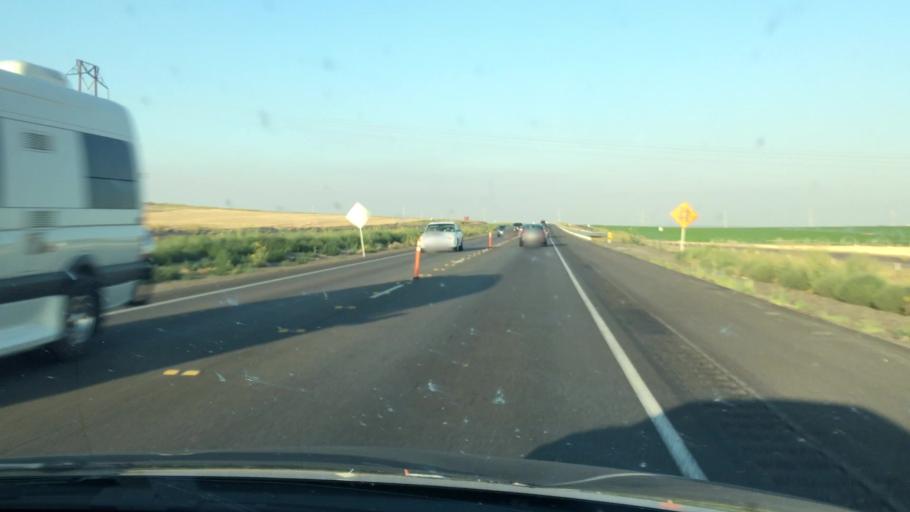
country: US
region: Idaho
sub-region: Twin Falls County
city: Hansen
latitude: 42.5761
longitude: -114.2419
